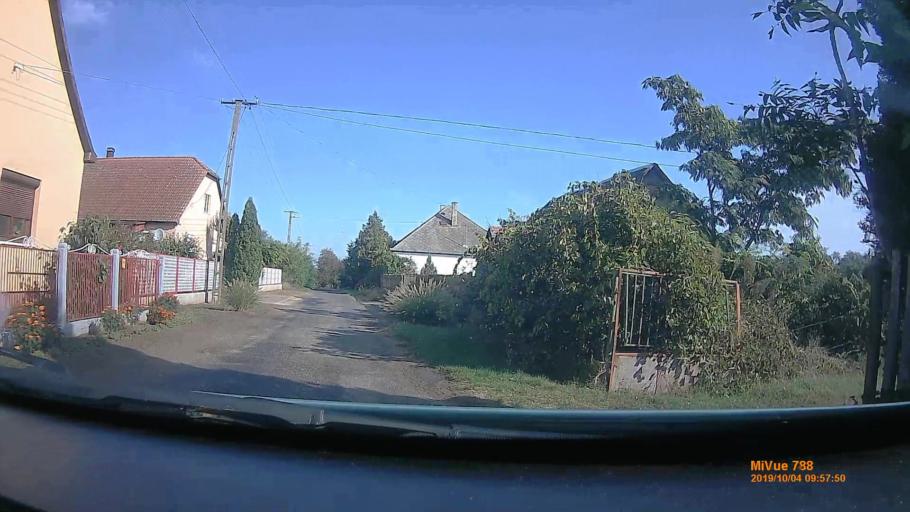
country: HU
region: Szabolcs-Szatmar-Bereg
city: Nyiregyhaza
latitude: 47.9408
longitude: 21.6635
